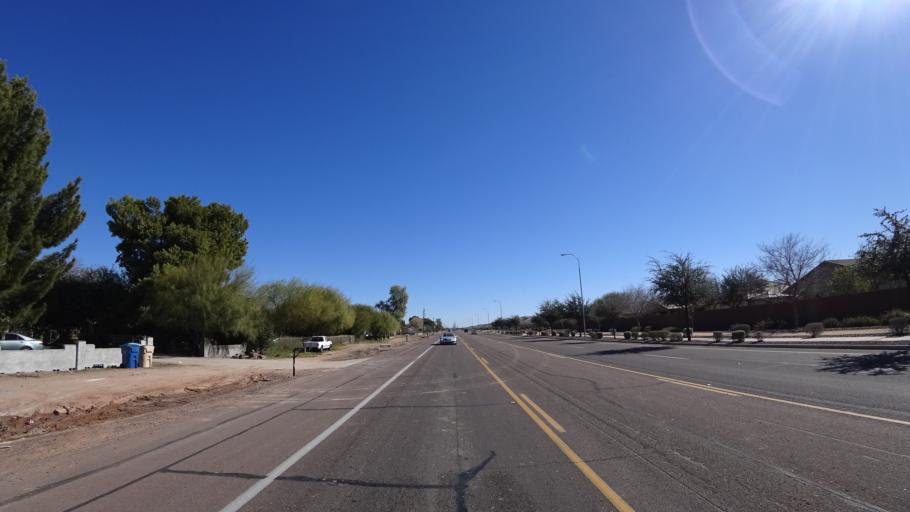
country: US
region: Arizona
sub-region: Maricopa County
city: Laveen
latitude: 33.3774
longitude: -112.2005
